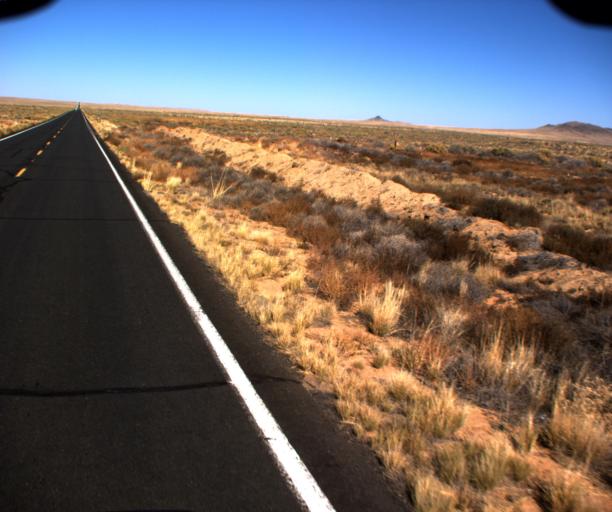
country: US
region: Arizona
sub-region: Navajo County
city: Dilkon
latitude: 35.5683
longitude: -110.4593
